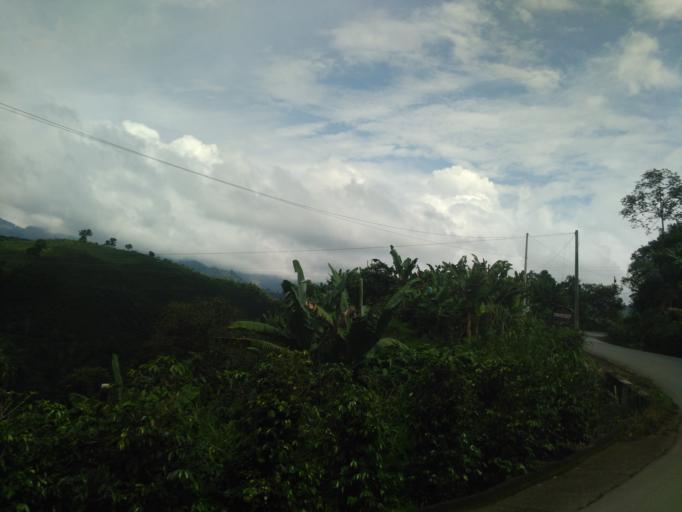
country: CO
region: Valle del Cauca
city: Sevilla
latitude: 4.3014
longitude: -75.8951
